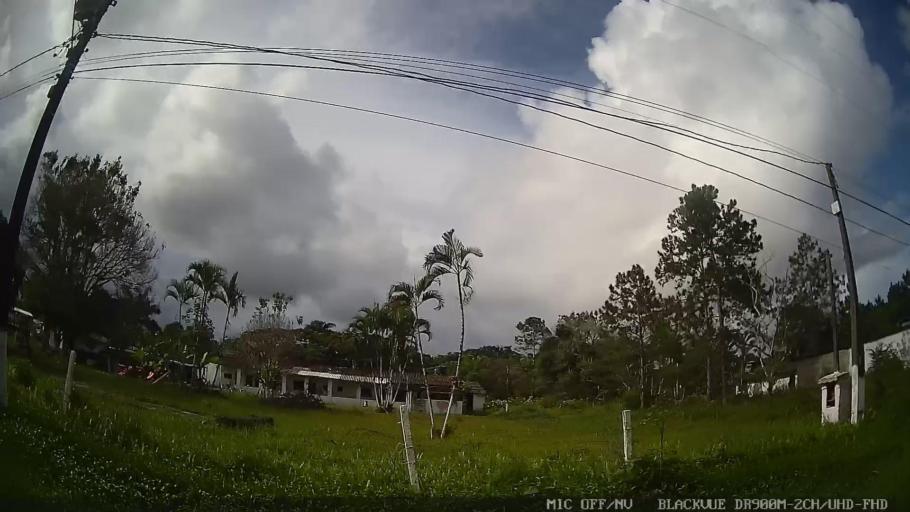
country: BR
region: Sao Paulo
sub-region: Itanhaem
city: Itanhaem
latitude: -24.2263
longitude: -46.8955
